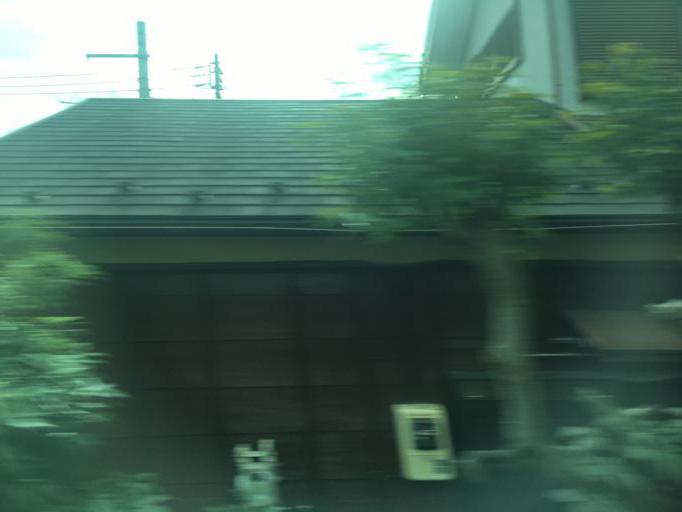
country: JP
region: Tokyo
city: Kokubunji
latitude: 35.6829
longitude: 139.4425
